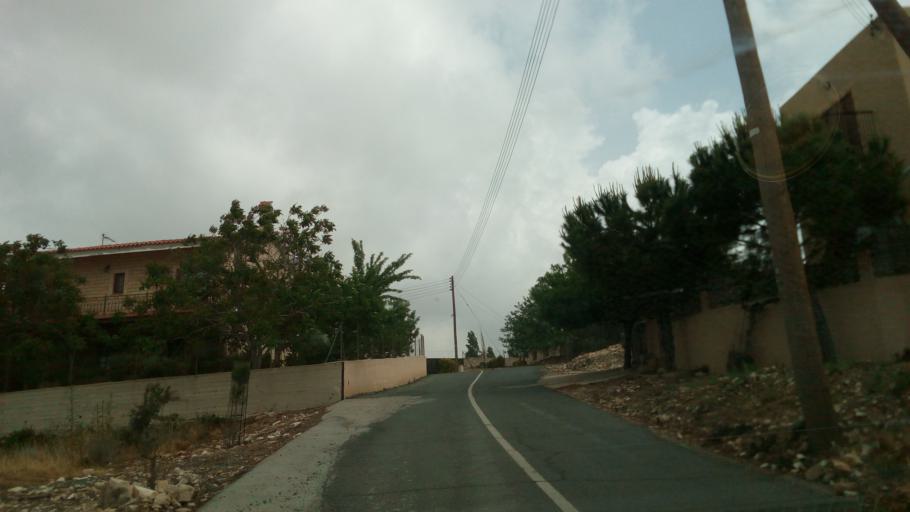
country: CY
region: Limassol
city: Pachna
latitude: 34.8154
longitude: 32.8705
